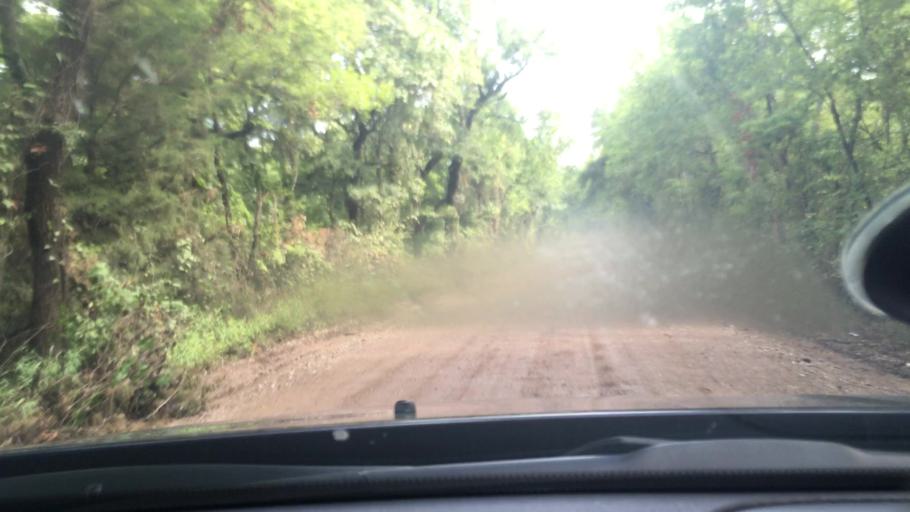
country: US
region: Oklahoma
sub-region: Atoka County
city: Atoka
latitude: 34.4482
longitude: -96.0676
